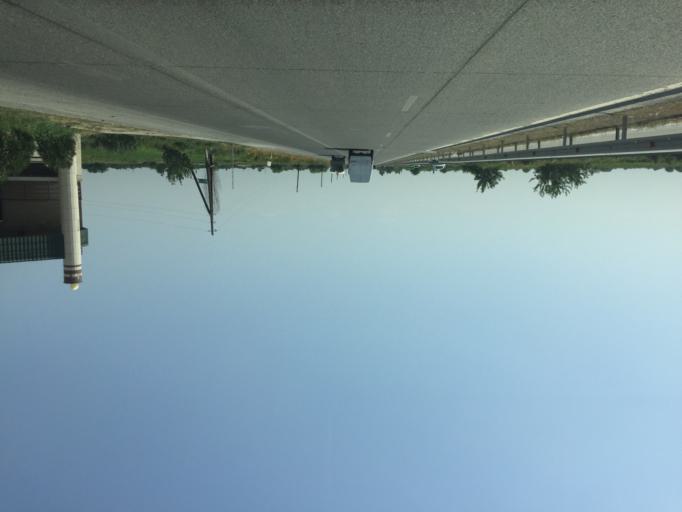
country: AM
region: Ararat
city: Berkanush
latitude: 39.9666
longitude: 44.5092
